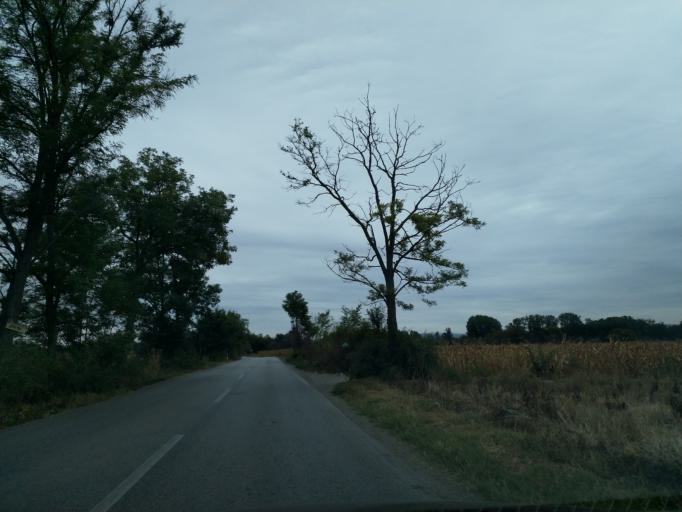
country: RS
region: Central Serbia
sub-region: Pomoravski Okrug
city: Paracin
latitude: 43.8410
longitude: 21.3738
